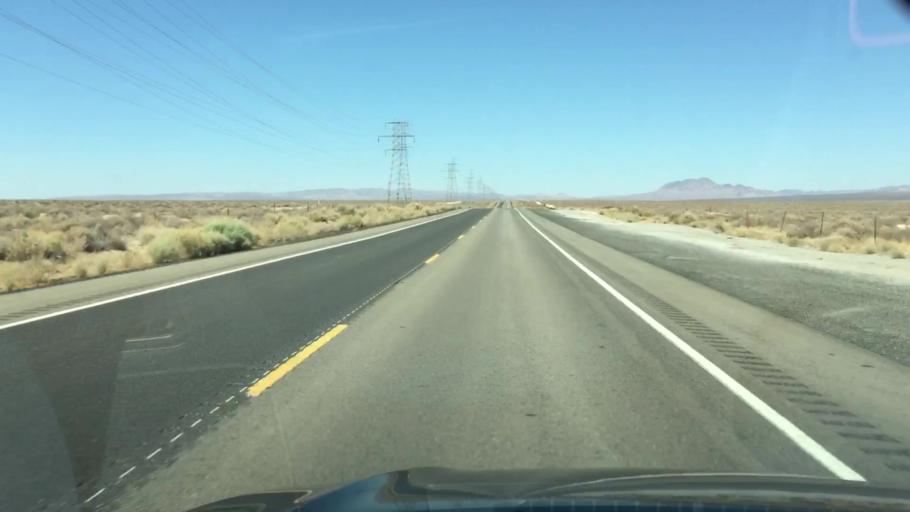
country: US
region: California
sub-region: Kern County
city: Boron
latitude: 35.1198
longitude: -117.5771
